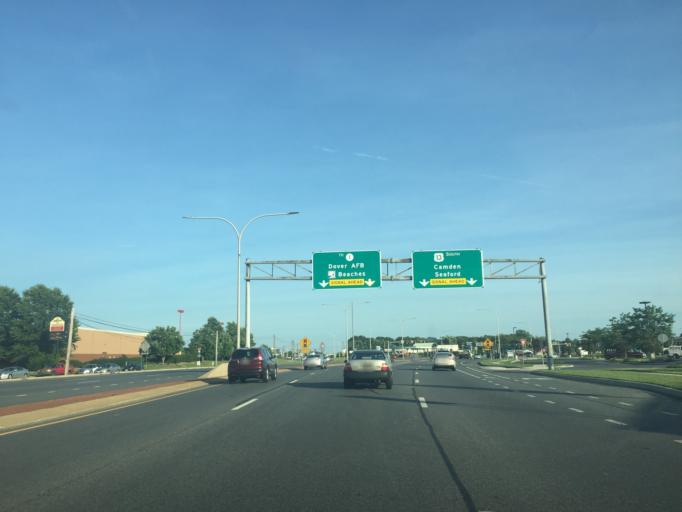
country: US
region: Delaware
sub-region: Kent County
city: Dover
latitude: 39.1607
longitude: -75.5131
